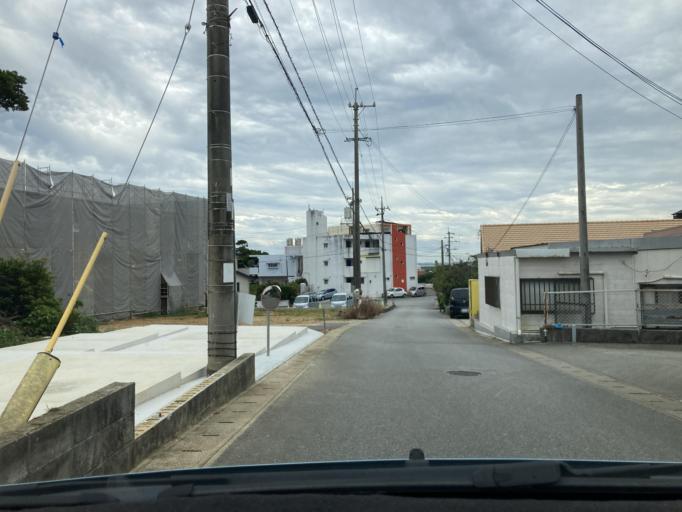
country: JP
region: Okinawa
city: Ishikawa
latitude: 26.4054
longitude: 127.7394
